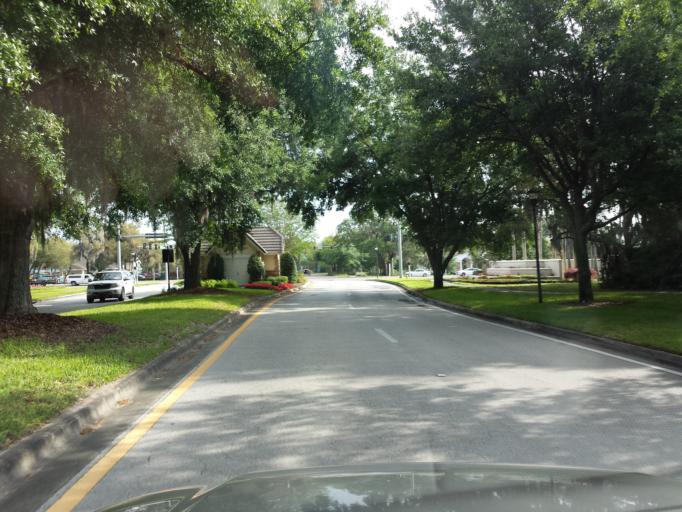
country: US
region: Florida
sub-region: Hillsborough County
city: Fish Hawk
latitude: 27.8524
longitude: -82.2316
